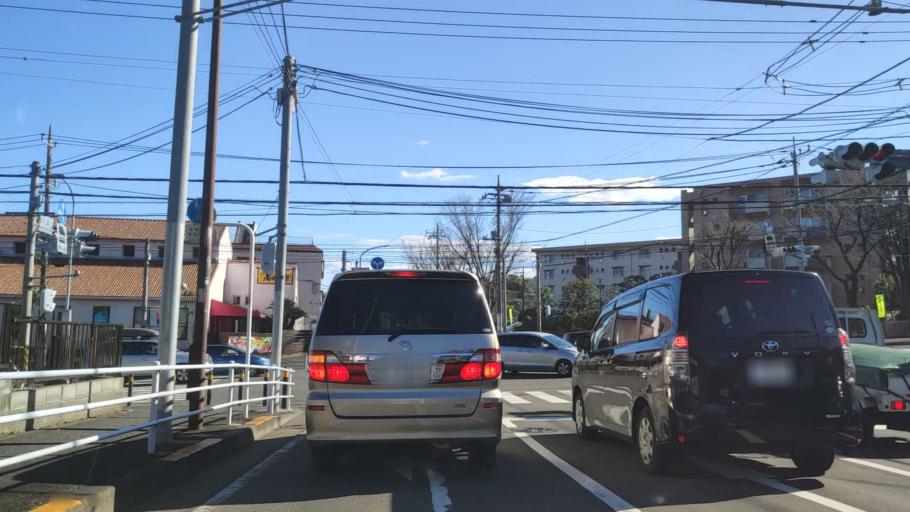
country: JP
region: Tokyo
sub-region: Machida-shi
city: Machida
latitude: 35.5158
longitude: 139.4994
